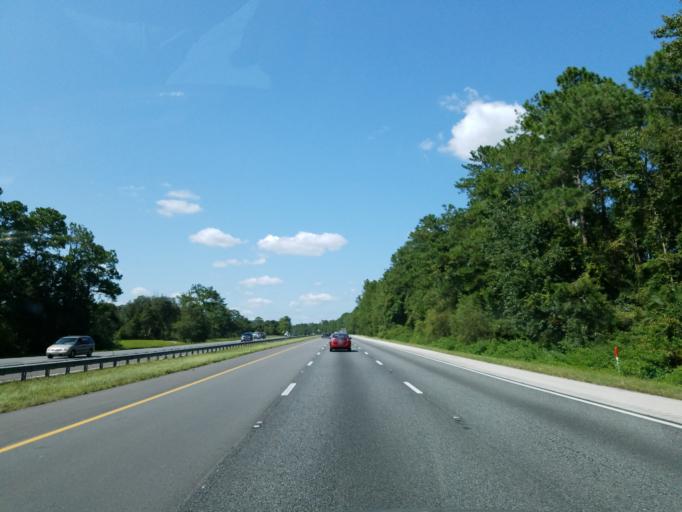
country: US
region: Florida
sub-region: Marion County
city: Citra
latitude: 29.4589
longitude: -82.2703
